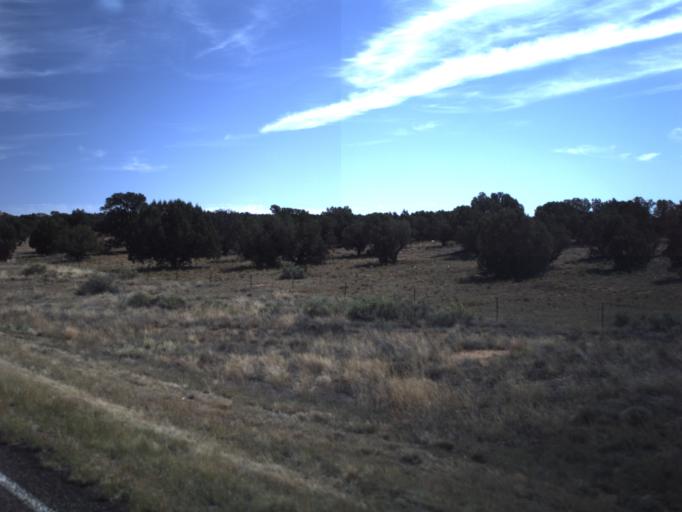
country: US
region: Utah
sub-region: Wayne County
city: Loa
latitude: 37.7487
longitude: -111.4901
